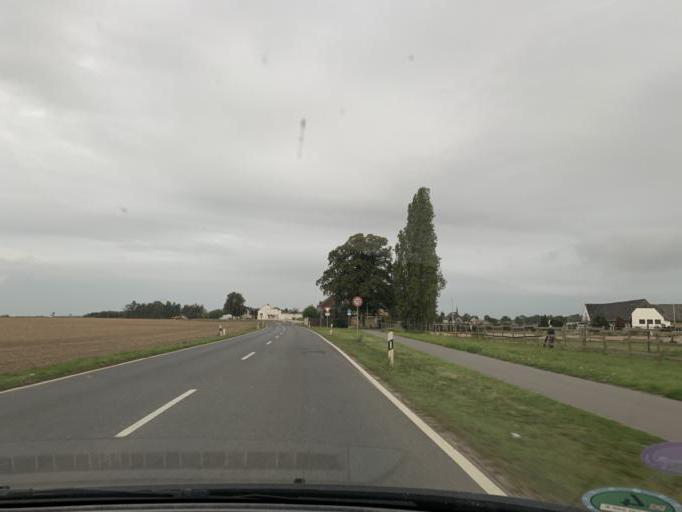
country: DE
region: North Rhine-Westphalia
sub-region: Regierungsbezirk Koln
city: Niederzier
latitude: 50.8383
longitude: 6.4306
